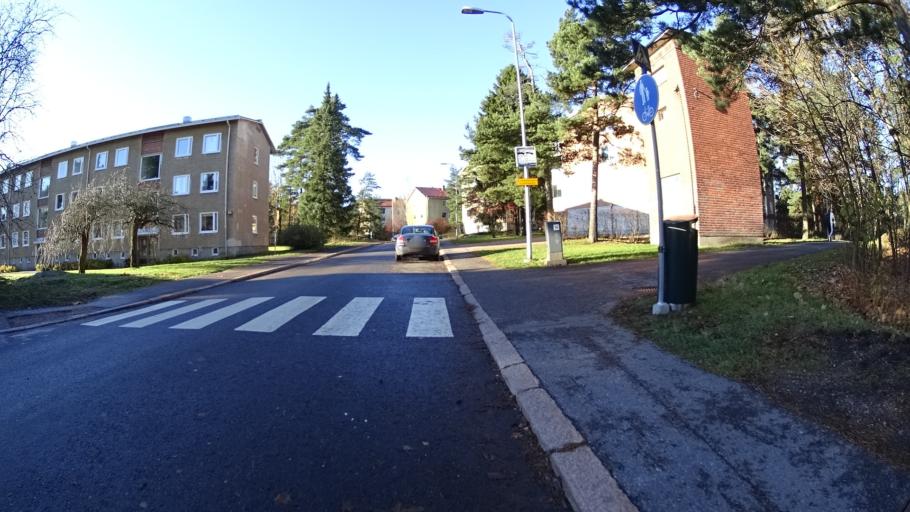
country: FI
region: Uusimaa
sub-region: Helsinki
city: Teekkarikylae
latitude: 60.2280
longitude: 24.8903
